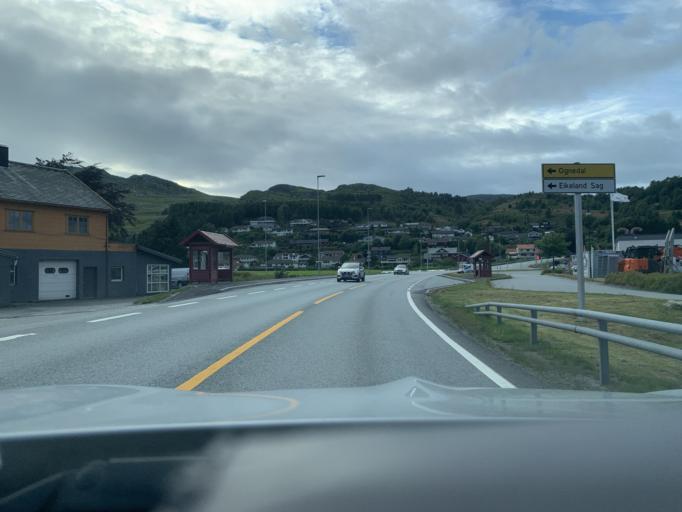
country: NO
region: Rogaland
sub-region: Bjerkreim
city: Vikesa
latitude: 58.6302
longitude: 6.0790
